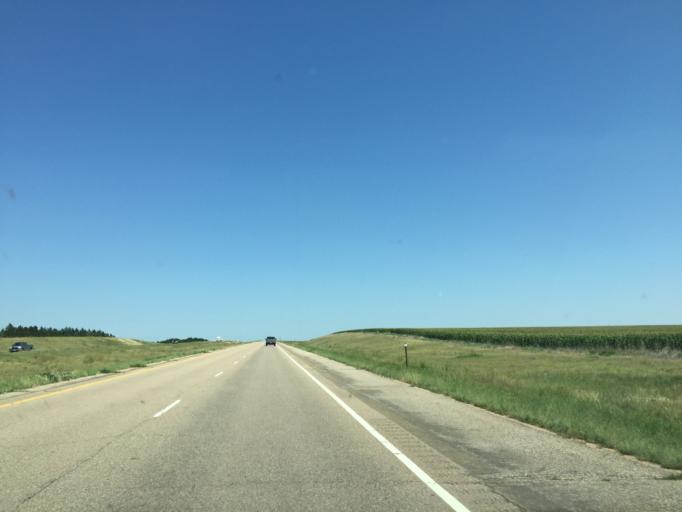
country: US
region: Colorado
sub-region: Kit Carson County
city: Burlington
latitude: 39.2941
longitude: -102.3534
